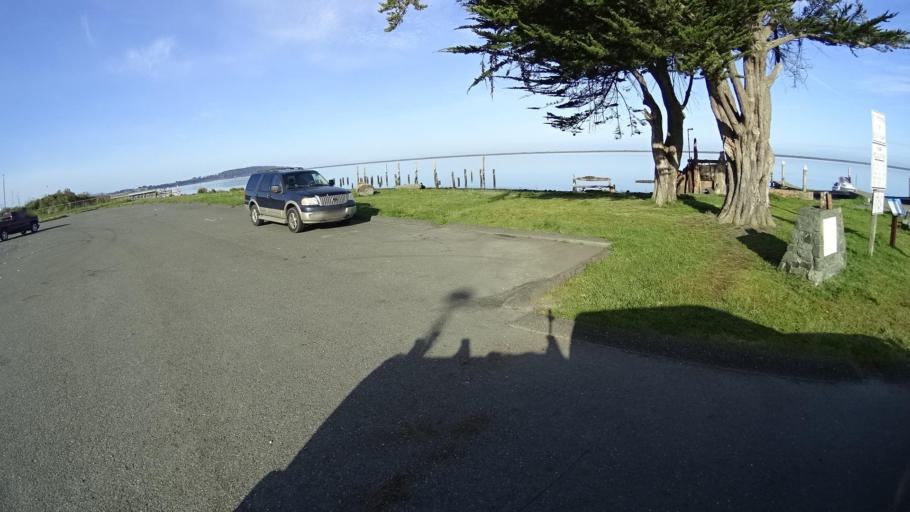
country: US
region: California
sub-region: Humboldt County
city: Humboldt Hill
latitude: 40.7259
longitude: -124.2209
